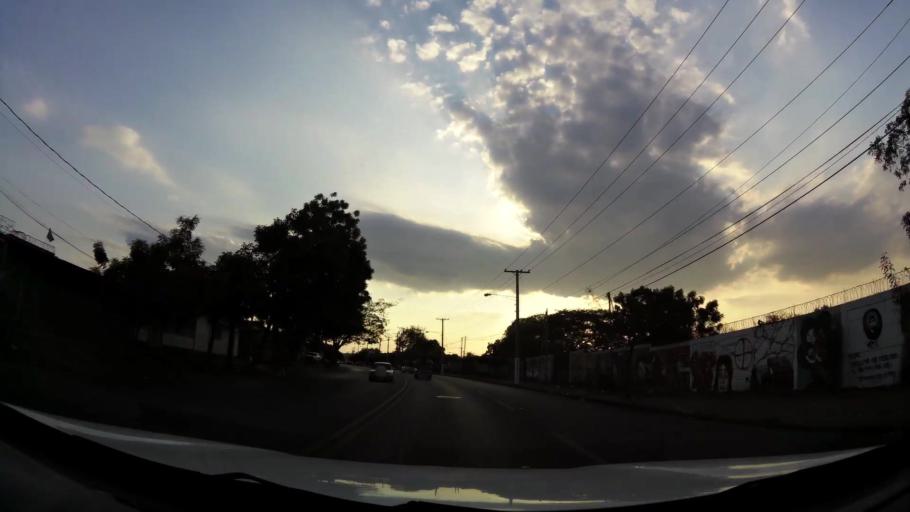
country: NI
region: Managua
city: Managua
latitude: 12.1464
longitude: -86.2470
